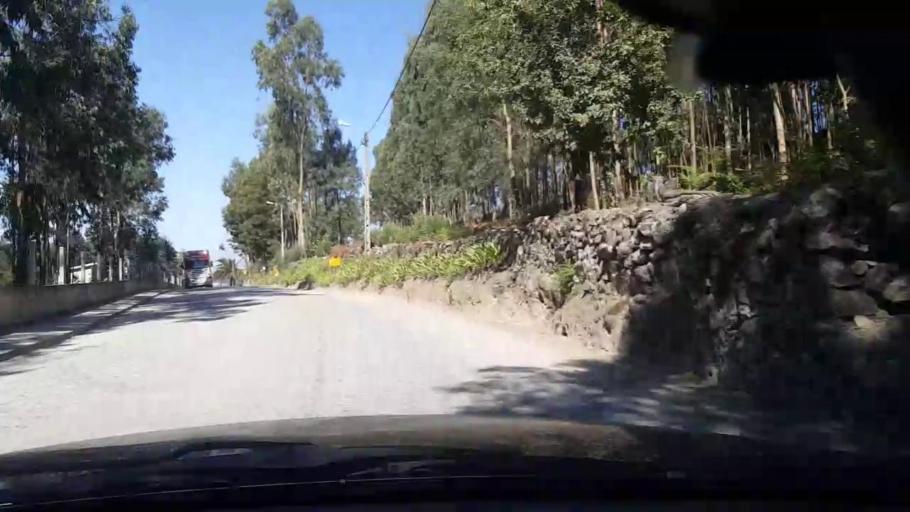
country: PT
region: Porto
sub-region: Maia
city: Gemunde
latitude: 41.3239
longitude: -8.6412
